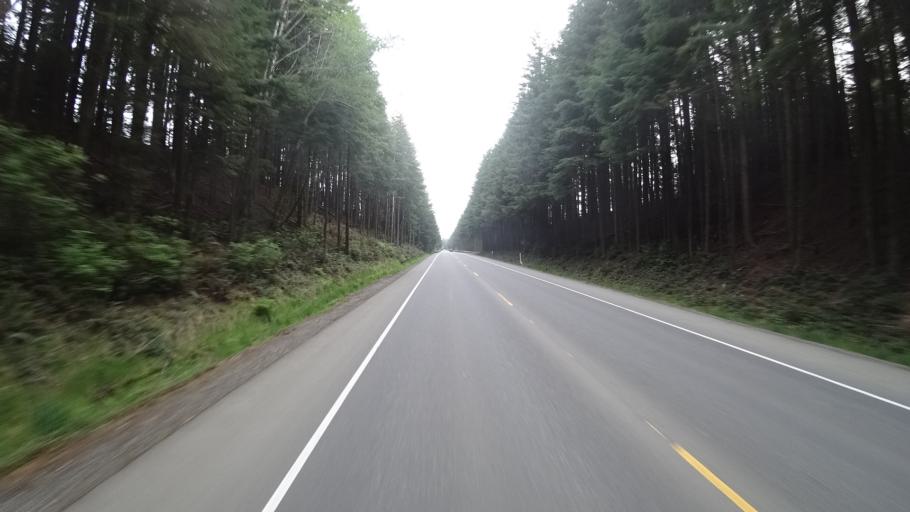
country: US
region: Oregon
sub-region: Coos County
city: Barview
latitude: 43.2430
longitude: -124.2880
